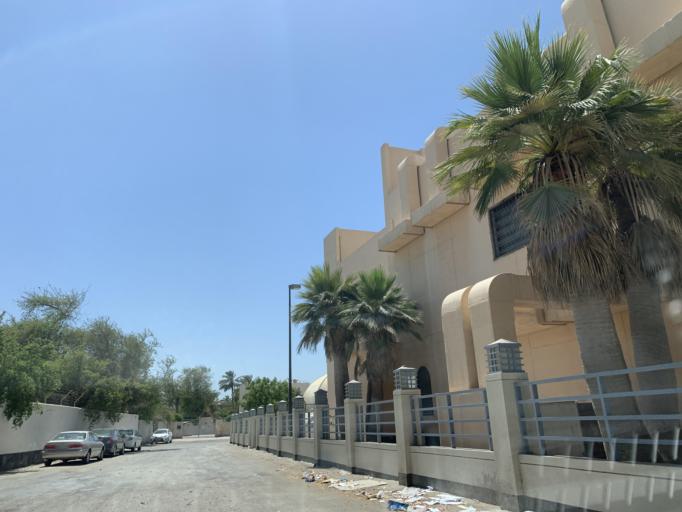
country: BH
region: Manama
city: Jidd Hafs
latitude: 26.2206
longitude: 50.4893
